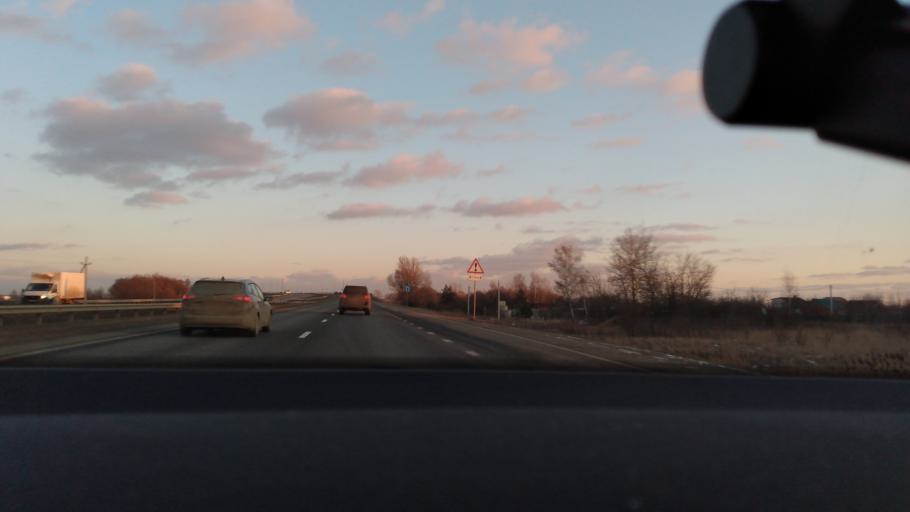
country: RU
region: Moskovskaya
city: Raduzhnyy
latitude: 55.1445
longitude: 38.7329
